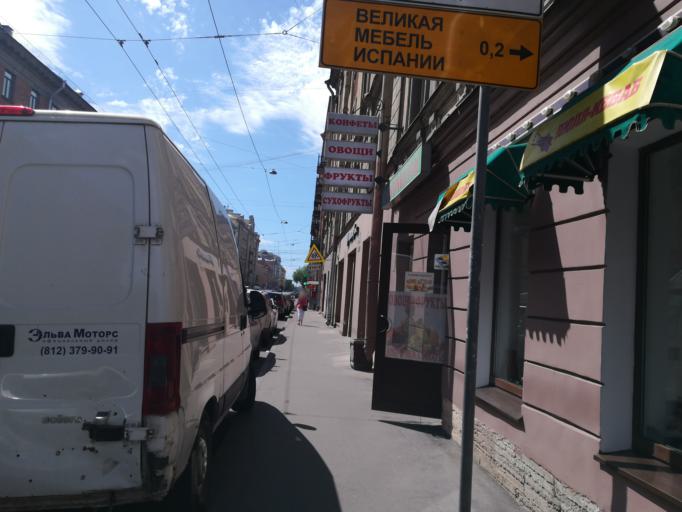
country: RU
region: St.-Petersburg
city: Vasyl'evsky Ostrov
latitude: 59.9452
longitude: 30.2680
